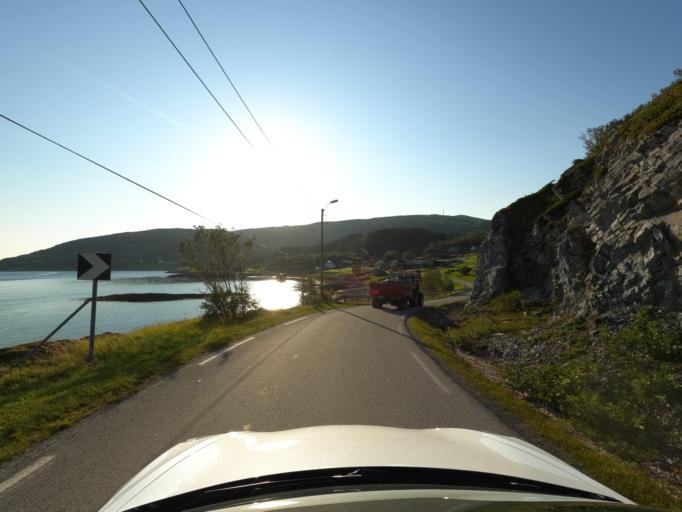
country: NO
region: Troms
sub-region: Skanland
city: Evenskjer
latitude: 68.4549
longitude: 16.6063
